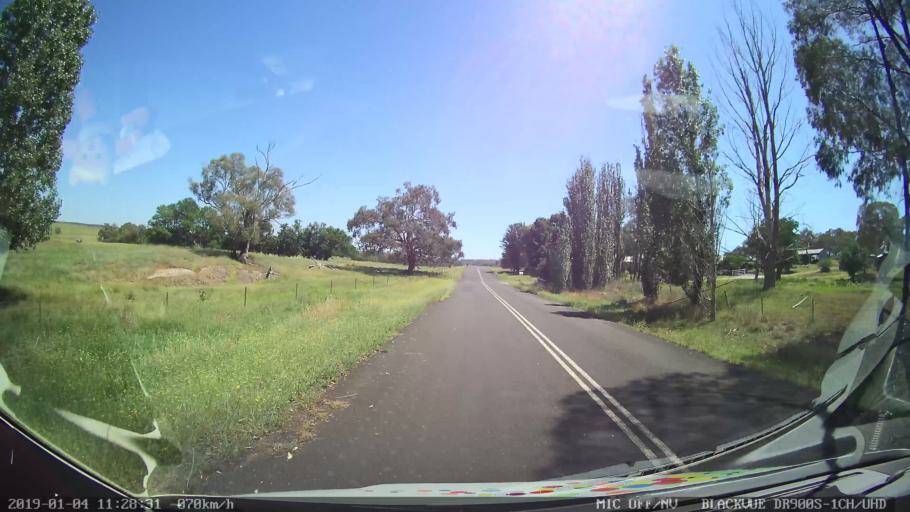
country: AU
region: New South Wales
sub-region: Cabonne
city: Molong
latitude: -33.0989
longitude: 148.7723
